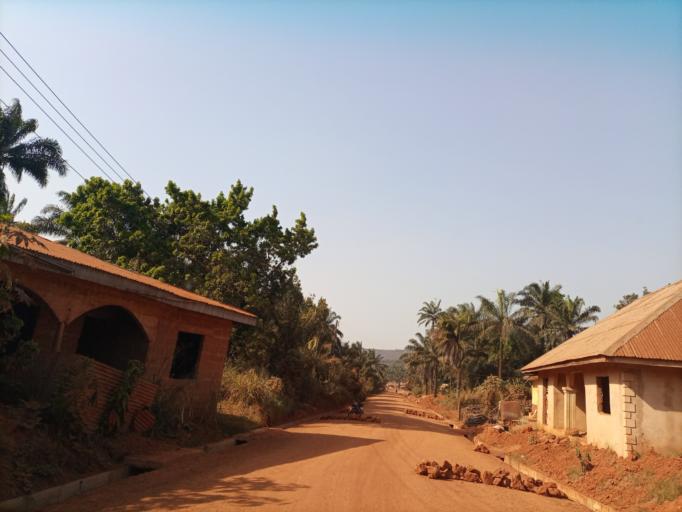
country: NG
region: Enugu
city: Aku
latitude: 6.6995
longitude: 7.3265
